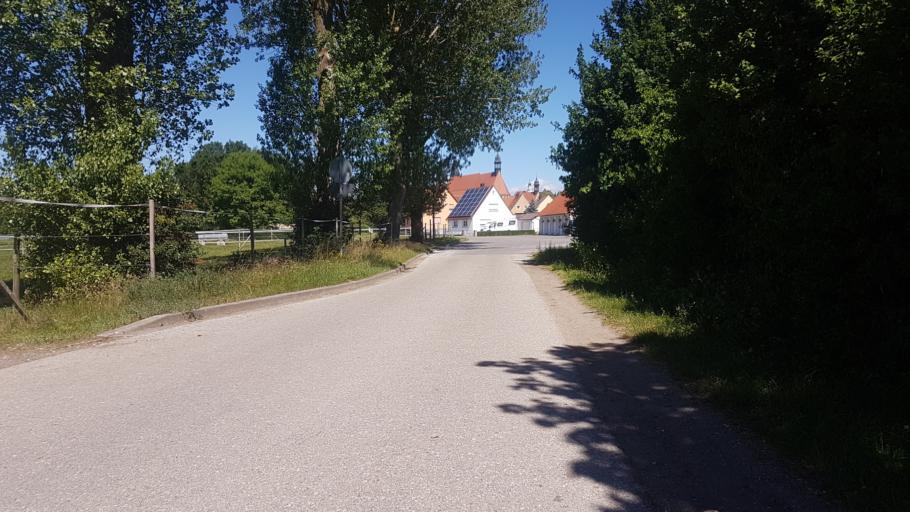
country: DE
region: Bavaria
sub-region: Regierungsbezirk Mittelfranken
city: Herrieden
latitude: 49.2296
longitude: 10.5011
